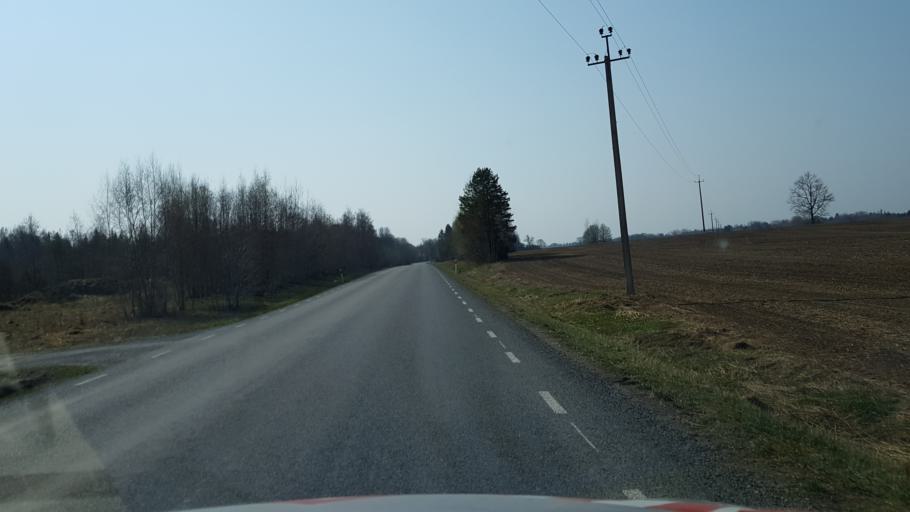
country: EE
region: Raplamaa
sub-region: Kehtna vald
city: Kehtna
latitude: 59.0473
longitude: 24.9462
